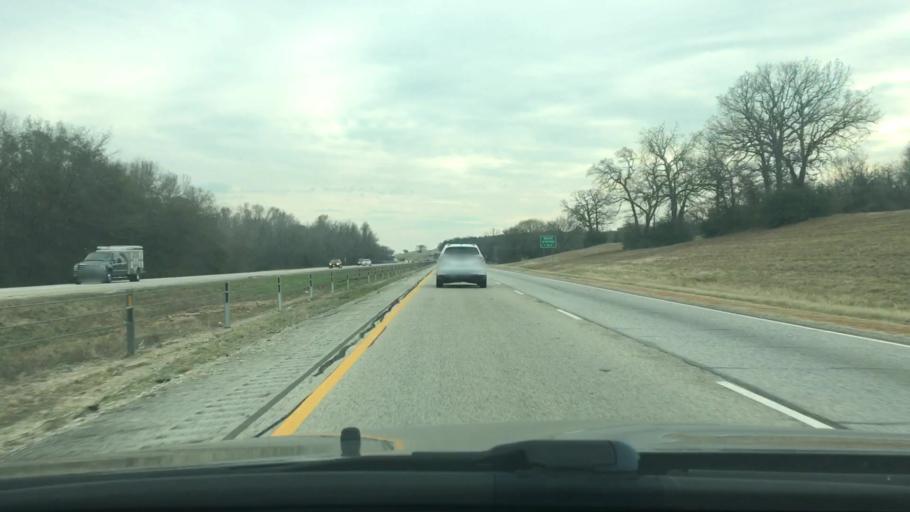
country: US
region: Texas
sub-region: Leon County
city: Centerville
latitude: 31.3005
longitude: -95.9999
